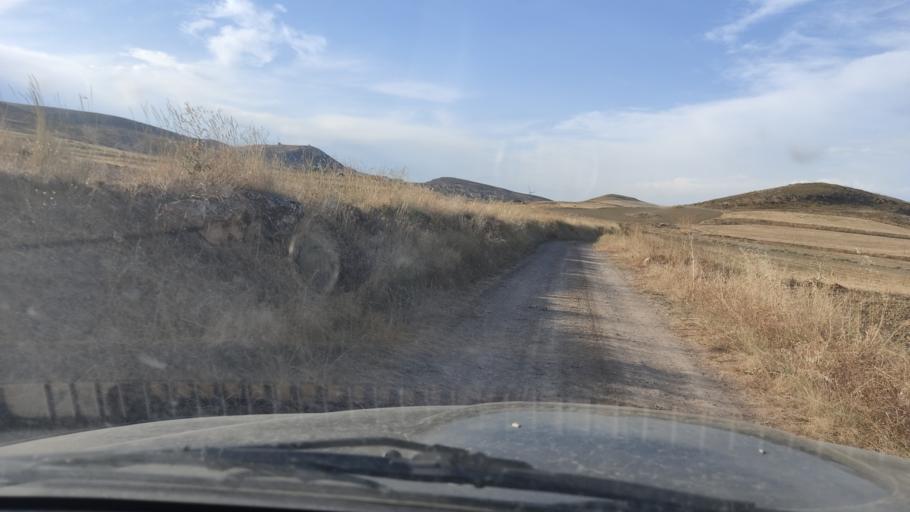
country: ES
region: Aragon
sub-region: Provincia de Teruel
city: Monforte de Moyuela
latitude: 41.0433
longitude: -1.0014
